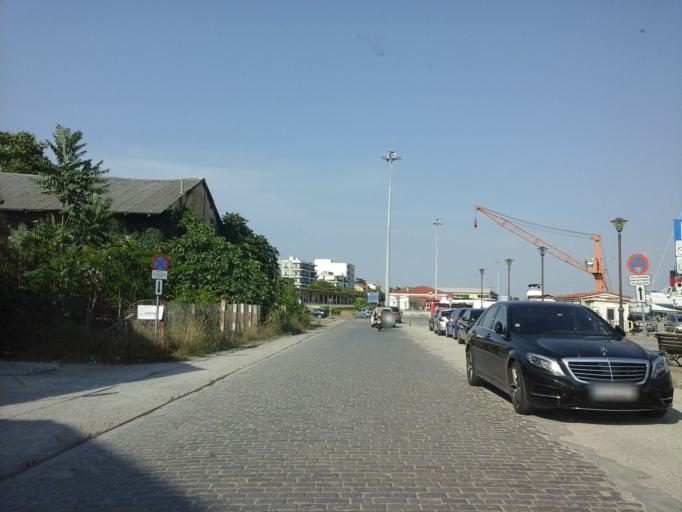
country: GR
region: East Macedonia and Thrace
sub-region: Nomos Evrou
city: Alexandroupoli
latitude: 40.8440
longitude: 25.8776
